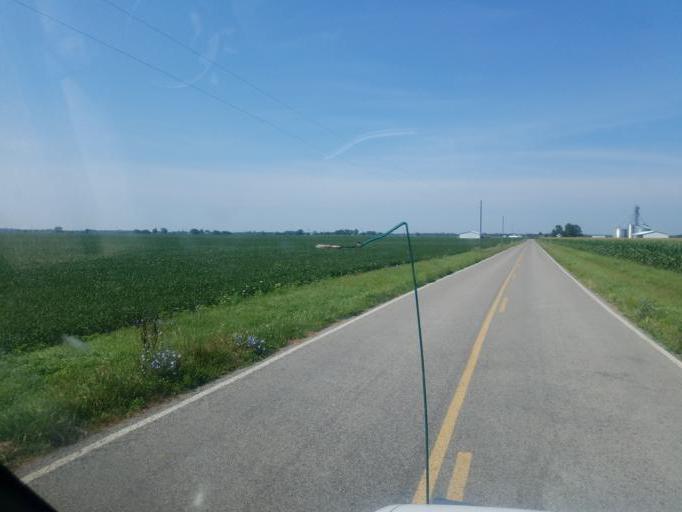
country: US
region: Ohio
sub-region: Champaign County
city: North Lewisburg
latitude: 40.2045
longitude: -83.5025
